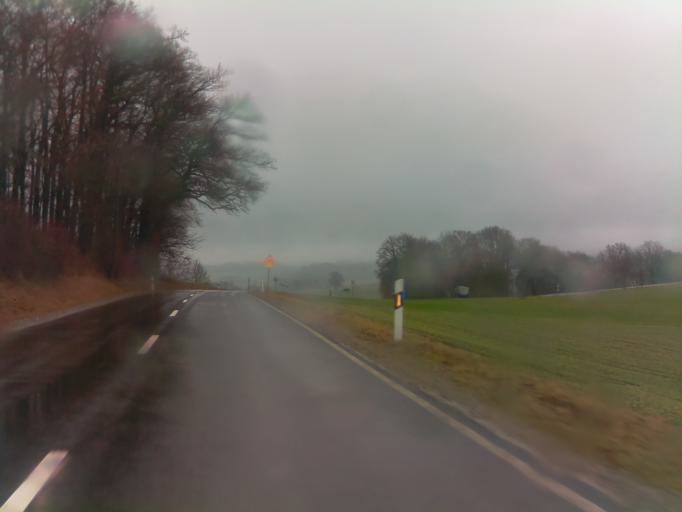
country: DE
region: Hesse
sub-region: Regierungsbezirk Kassel
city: Dipperz
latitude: 50.5132
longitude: 9.8154
